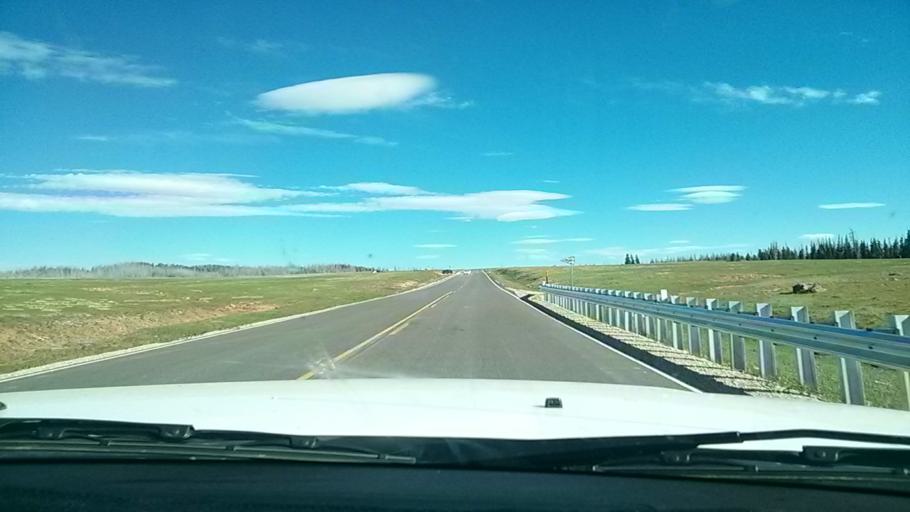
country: US
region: Utah
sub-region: Iron County
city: Parowan
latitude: 37.6718
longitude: -112.8409
